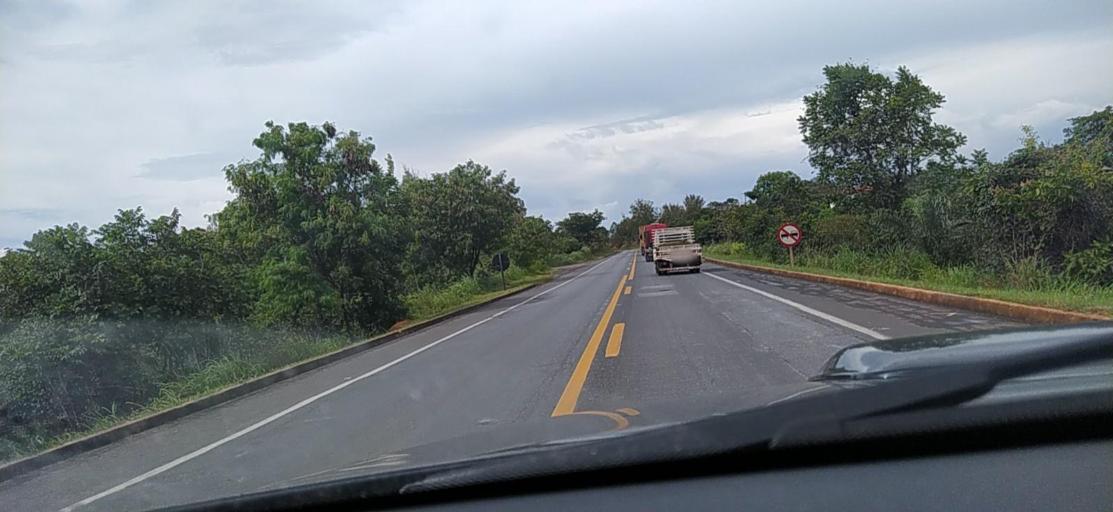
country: BR
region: Minas Gerais
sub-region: Montes Claros
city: Montes Claros
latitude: -16.8419
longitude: -43.8499
